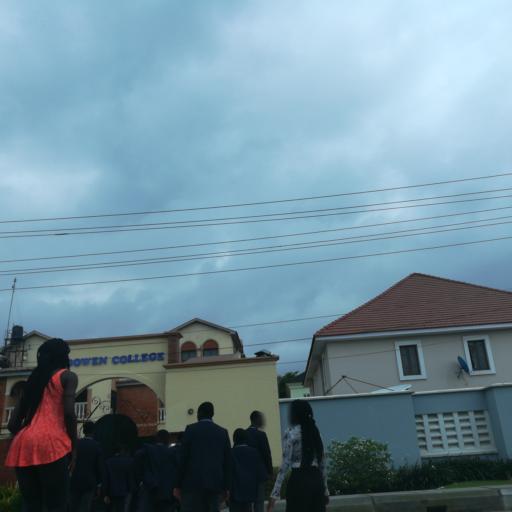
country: NG
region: Lagos
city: Ikoyi
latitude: 6.4371
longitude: 3.4646
